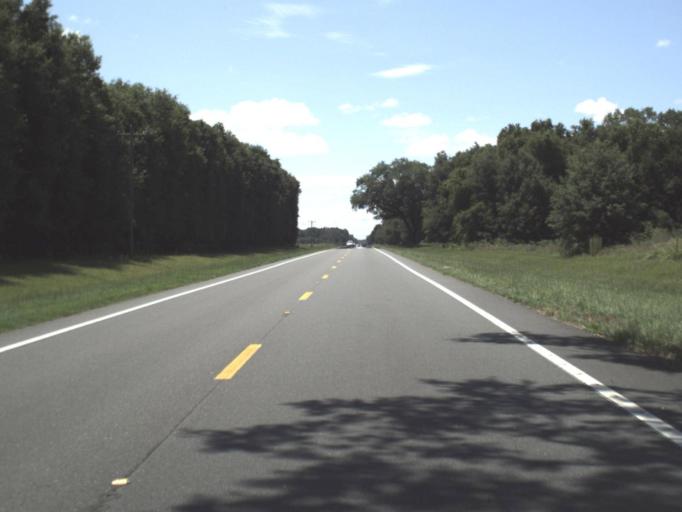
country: US
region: Florida
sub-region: Lafayette County
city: Mayo
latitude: 30.1020
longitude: -83.2422
